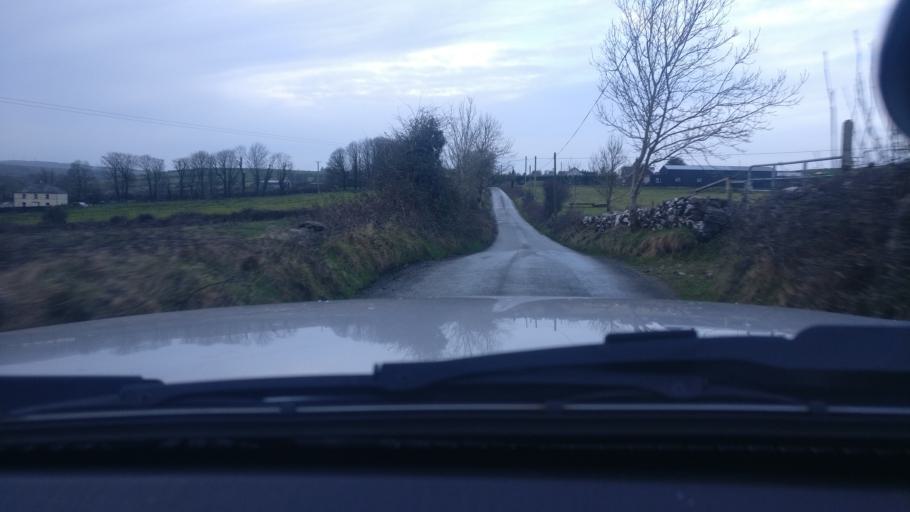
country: IE
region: Connaught
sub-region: County Galway
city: Loughrea
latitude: 53.1639
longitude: -8.5361
